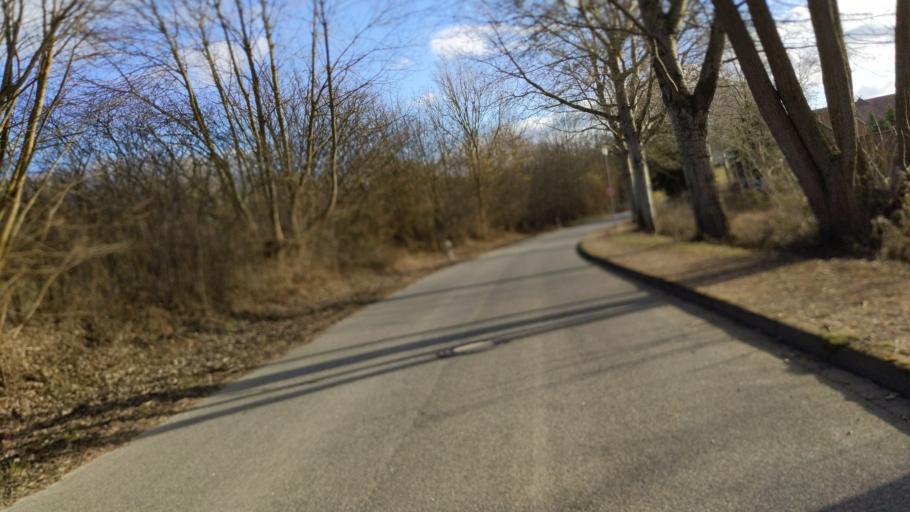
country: DE
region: Schleswig-Holstein
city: Scharbeutz
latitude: 54.0134
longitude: 10.7532
